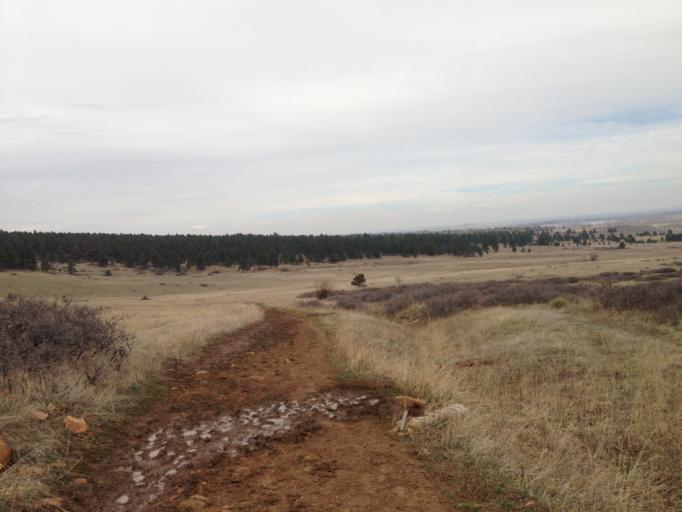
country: US
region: Colorado
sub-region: Boulder County
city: Boulder
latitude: 39.9511
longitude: -105.2662
